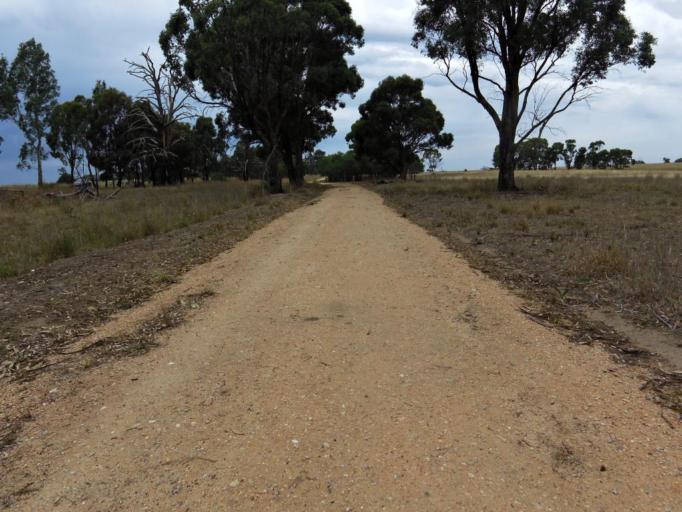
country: AU
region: Victoria
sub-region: Greater Bendigo
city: Kennington
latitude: -36.8514
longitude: 144.6135
